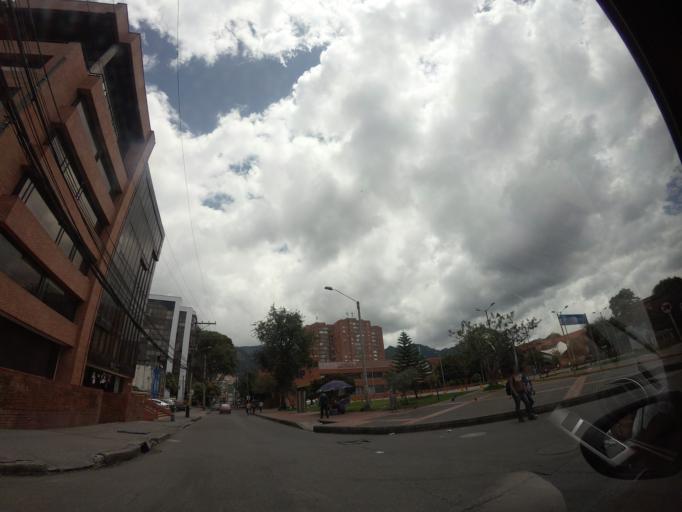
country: CO
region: Bogota D.C.
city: Barrio San Luis
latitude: 4.6659
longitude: -74.0588
